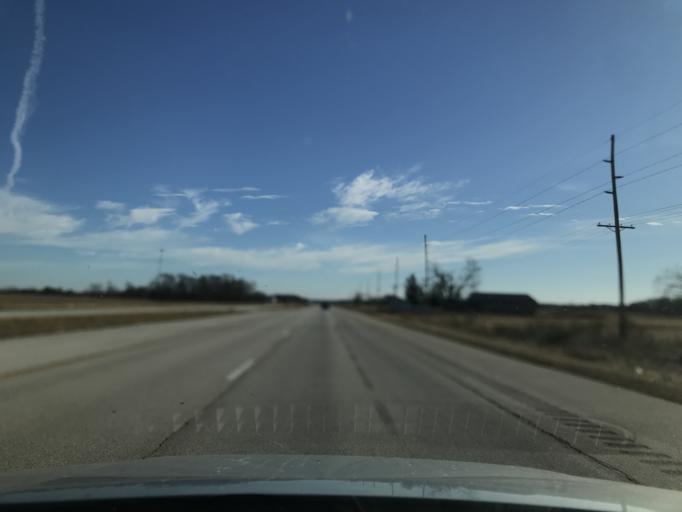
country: US
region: Illinois
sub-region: Hancock County
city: Carthage
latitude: 40.4148
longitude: -91.0453
